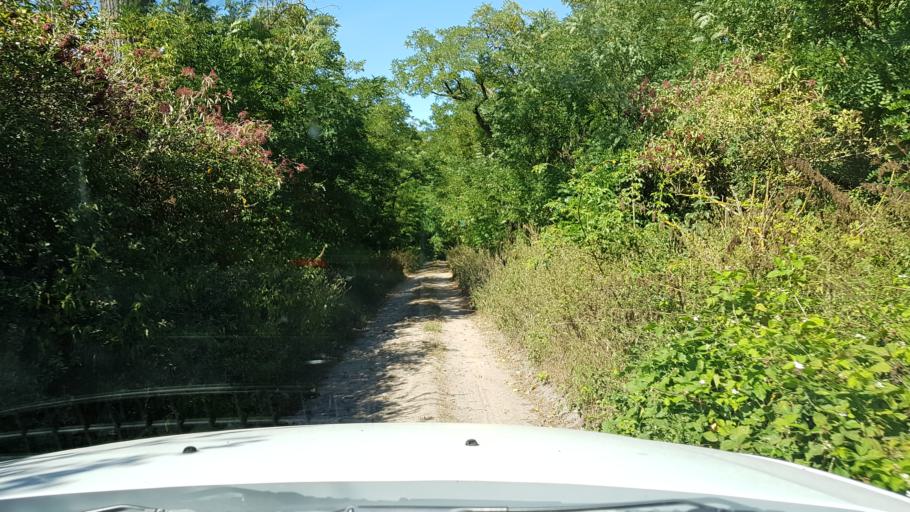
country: PL
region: West Pomeranian Voivodeship
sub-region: Powiat gryfinski
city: Cedynia
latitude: 52.8548
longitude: 14.2266
